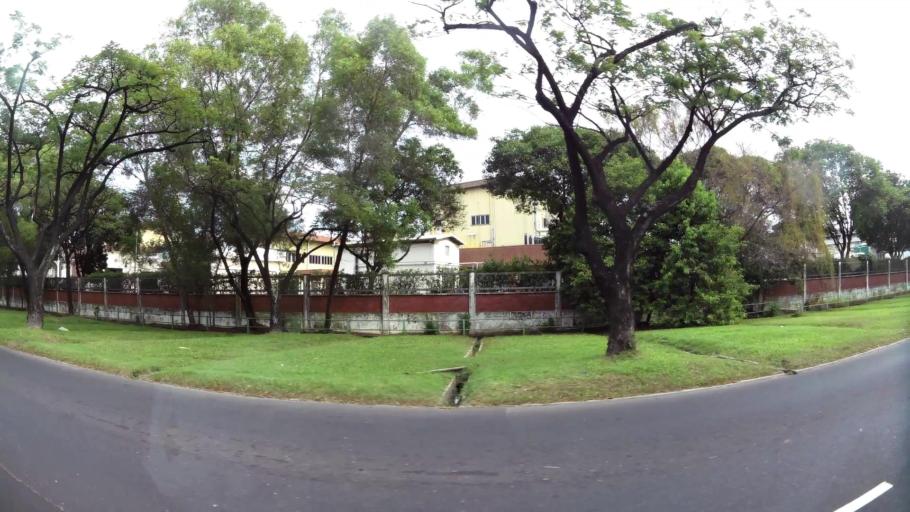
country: MY
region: Johor
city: Johor Bahru
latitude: 1.3080
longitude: 103.6635
